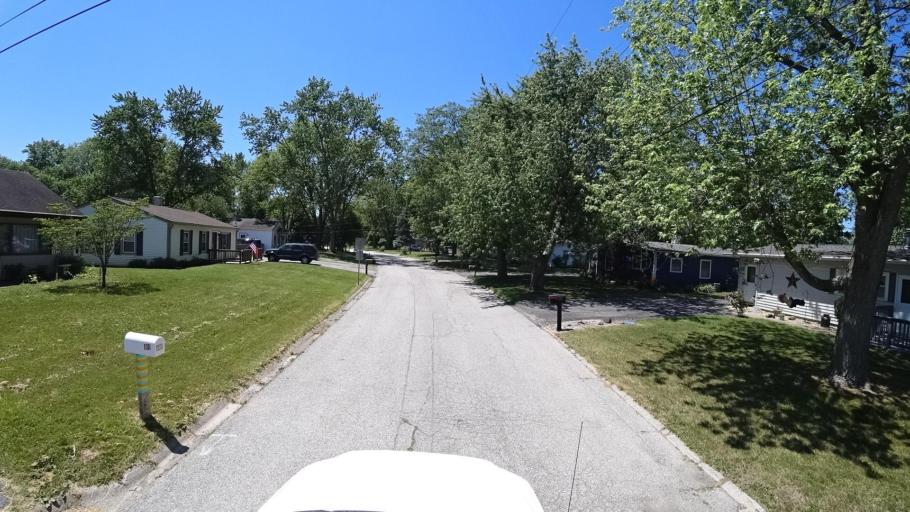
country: US
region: Indiana
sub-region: Porter County
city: Chesterton
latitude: 41.6187
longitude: -87.0594
